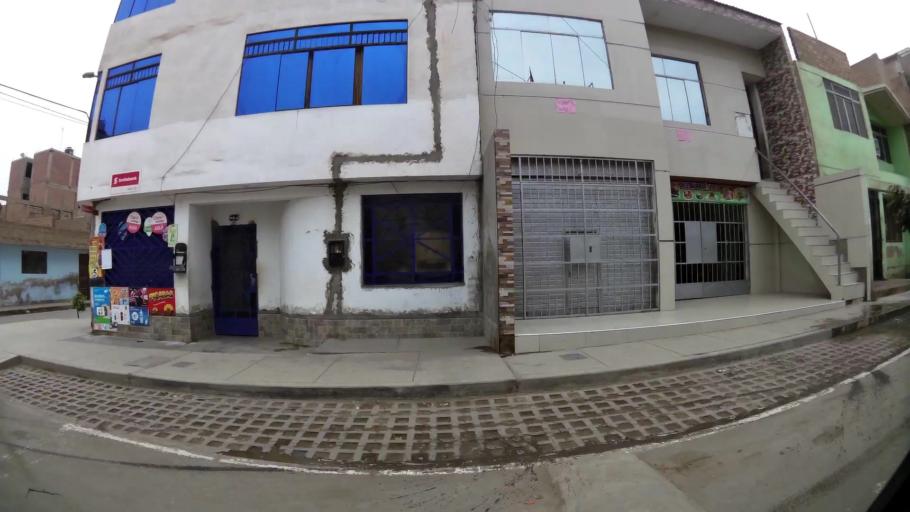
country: PE
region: Lima
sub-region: Lima
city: Urb. Santo Domingo
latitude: -11.8892
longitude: -77.0664
